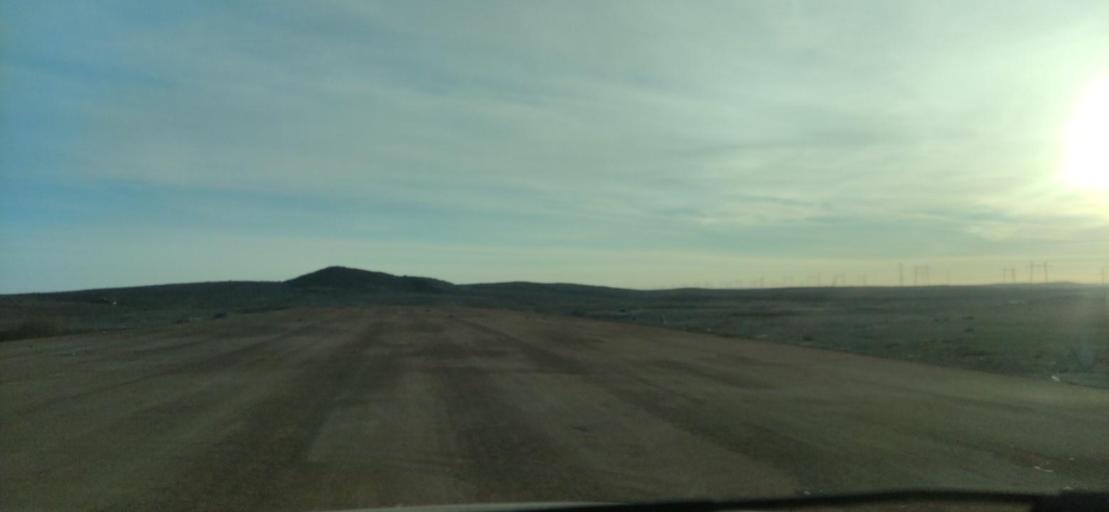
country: KZ
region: Qaraghandy
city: Saryshaghan
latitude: 46.1185
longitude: 73.5947
